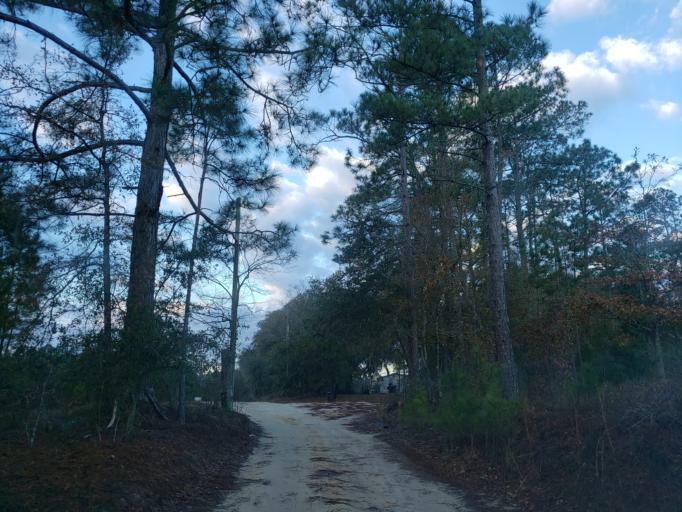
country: US
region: Georgia
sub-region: Chatham County
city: Bloomingdale
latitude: 32.1152
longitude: -81.3512
